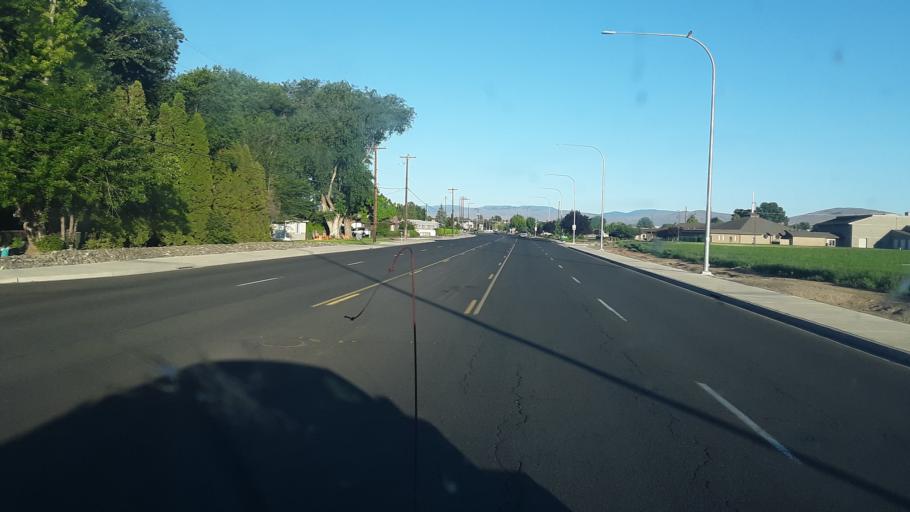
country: US
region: Washington
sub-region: Yakima County
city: West Valley
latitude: 46.5858
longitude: -120.5996
